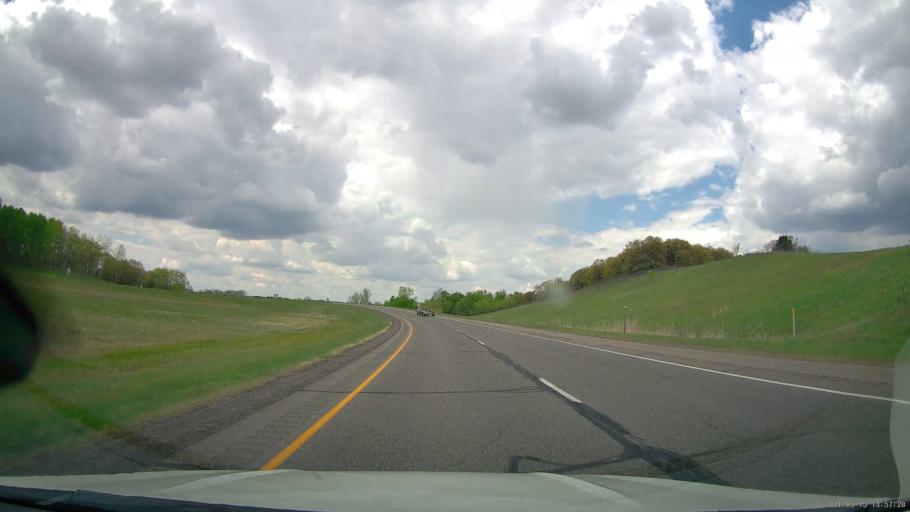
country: US
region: Minnesota
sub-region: Morrison County
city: Little Falls
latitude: 45.9958
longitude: -94.3426
